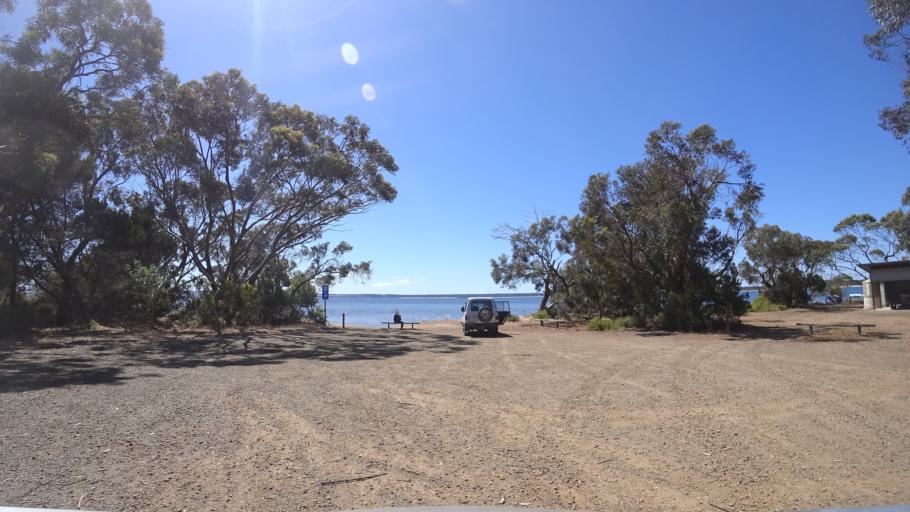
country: AU
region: South Australia
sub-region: Kangaroo Island
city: Kingscote
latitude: -35.7740
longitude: 137.7811
